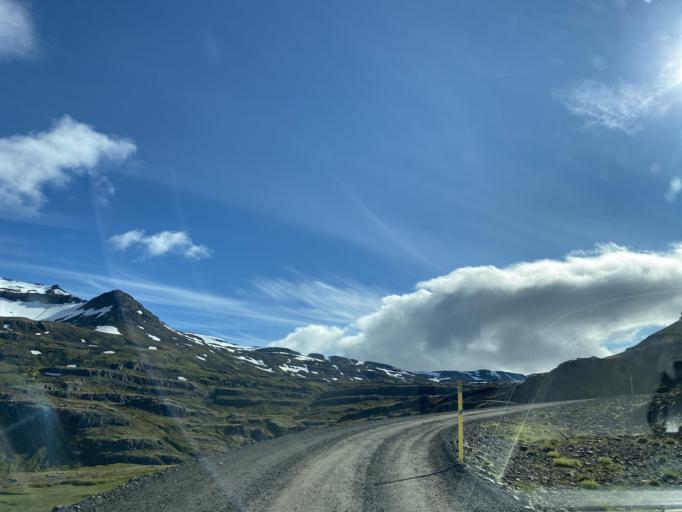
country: IS
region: East
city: Eskifjoerdur
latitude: 65.1801
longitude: -14.0908
